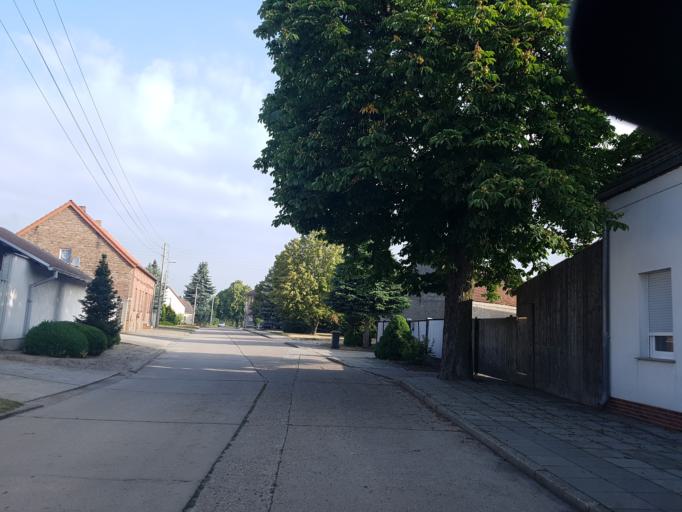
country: DE
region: Saxony-Anhalt
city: Holzdorf
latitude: 51.8573
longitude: 13.1042
